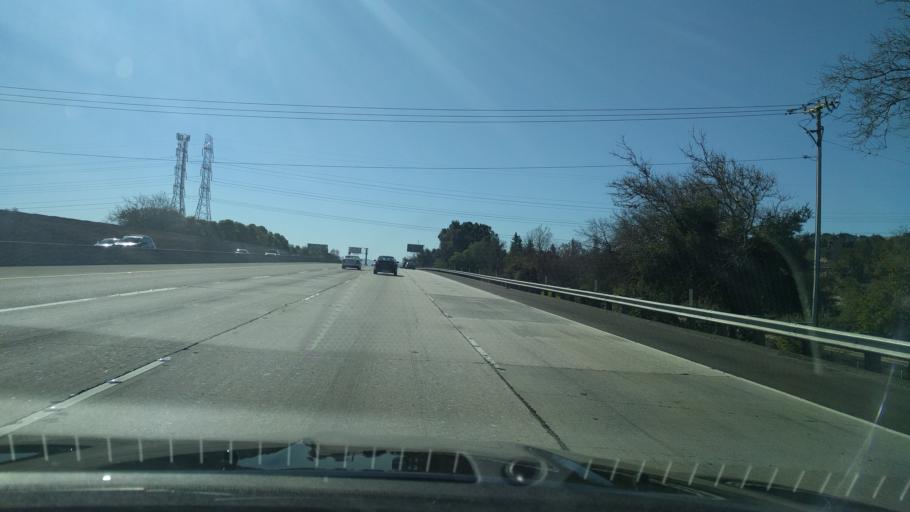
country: US
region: California
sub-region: Alameda County
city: Dublin
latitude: 37.7391
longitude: -121.9522
